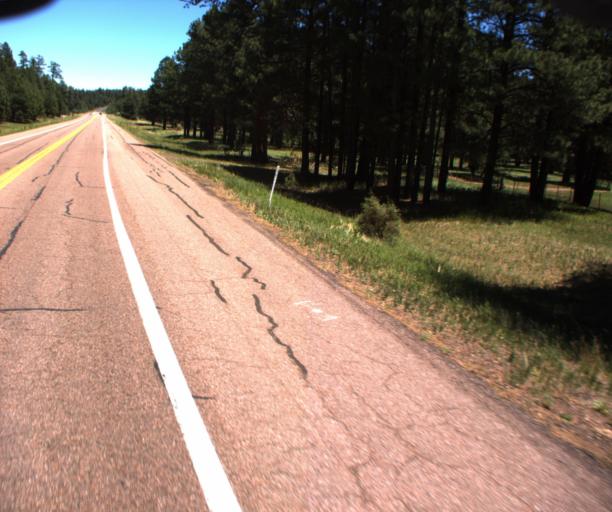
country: US
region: Arizona
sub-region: Gila County
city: Pine
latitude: 34.5465
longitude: -111.3209
